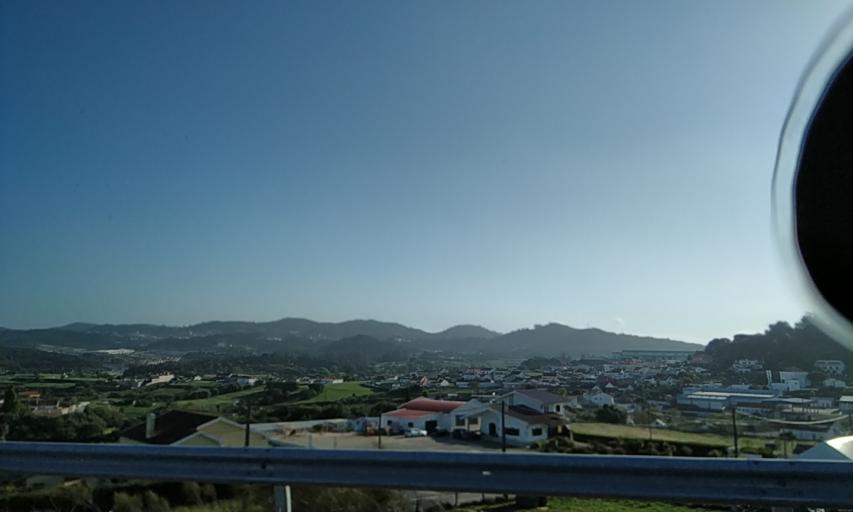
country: PT
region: Lisbon
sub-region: Mafra
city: Milharado
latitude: 38.9493
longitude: -9.2115
